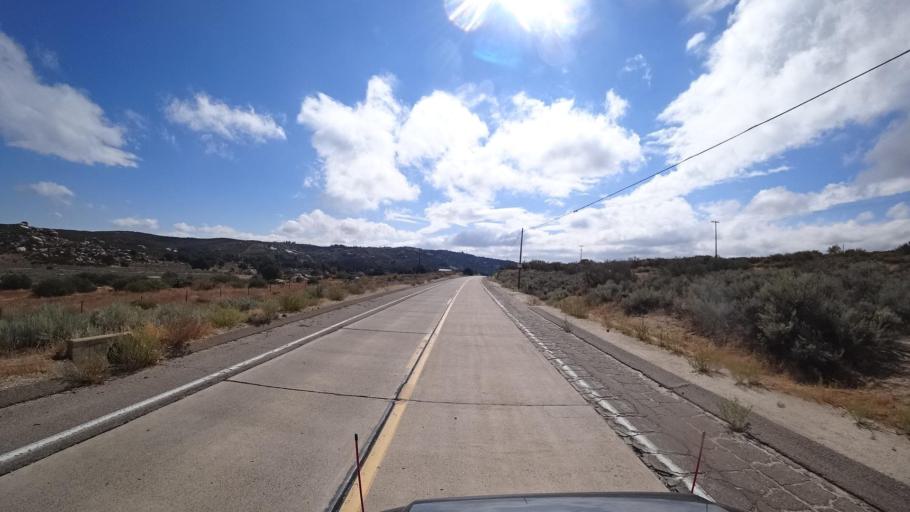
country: US
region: California
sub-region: San Diego County
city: Campo
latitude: 32.6934
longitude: -116.3431
